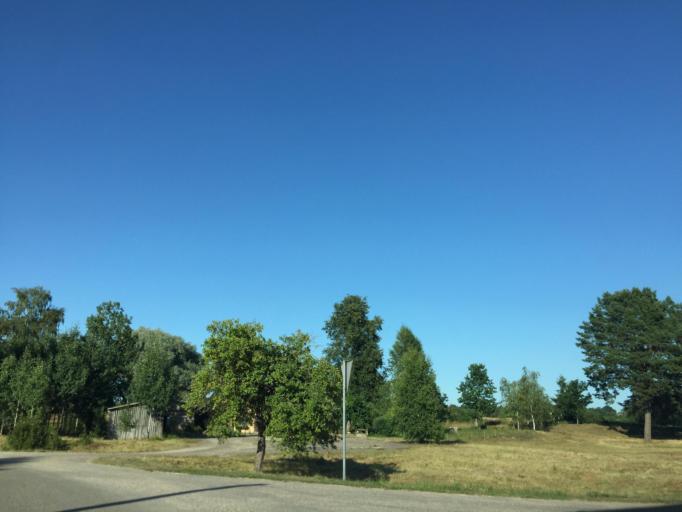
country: LV
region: Talsu Rajons
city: Sabile
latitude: 57.1334
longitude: 22.6501
